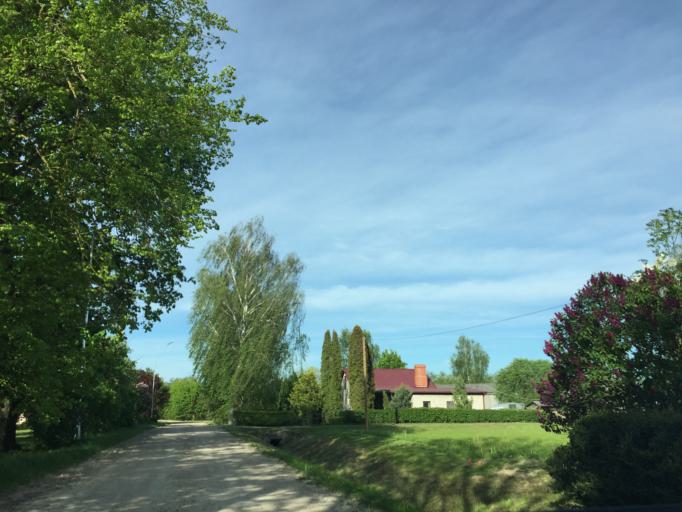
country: LV
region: Bauskas Rajons
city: Bauska
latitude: 56.4645
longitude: 24.1688
